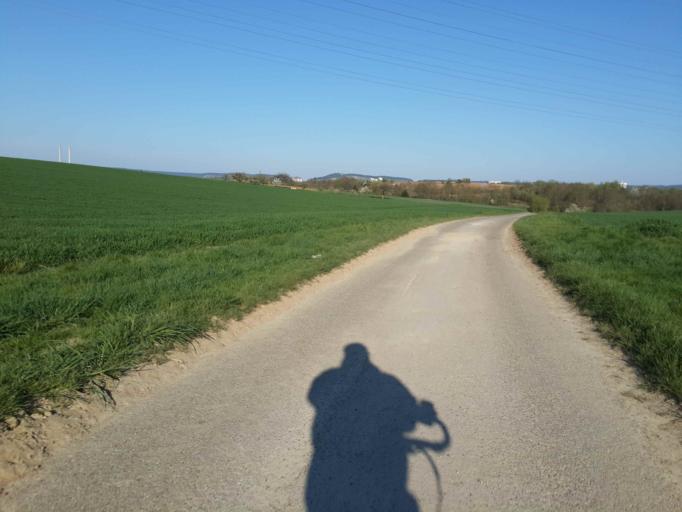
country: DE
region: Baden-Wuerttemberg
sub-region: Regierungsbezirk Stuttgart
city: Leingarten
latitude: 49.1524
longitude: 9.1484
